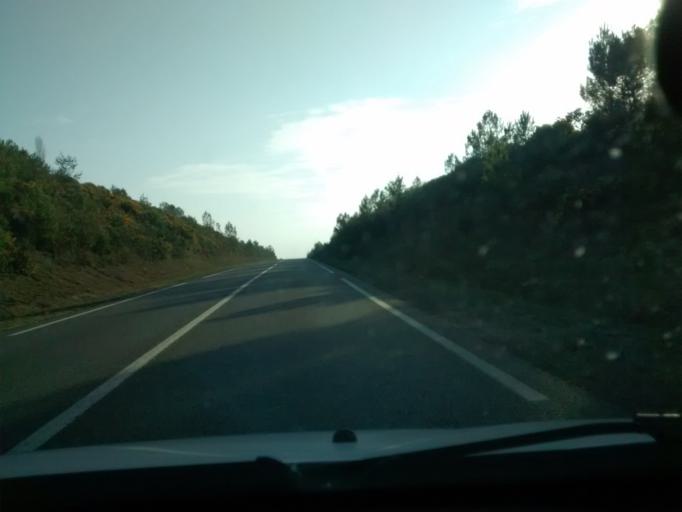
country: FR
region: Brittany
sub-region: Departement d'Ille-et-Vilaine
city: Chasne-sur-Illet
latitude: 48.2679
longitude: -1.5989
